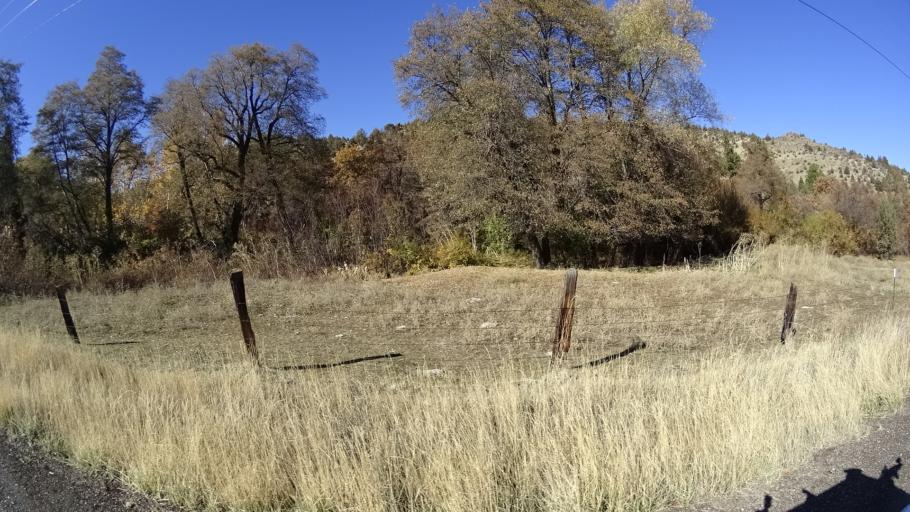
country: US
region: California
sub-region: Siskiyou County
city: Weed
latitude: 41.4775
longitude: -122.5751
